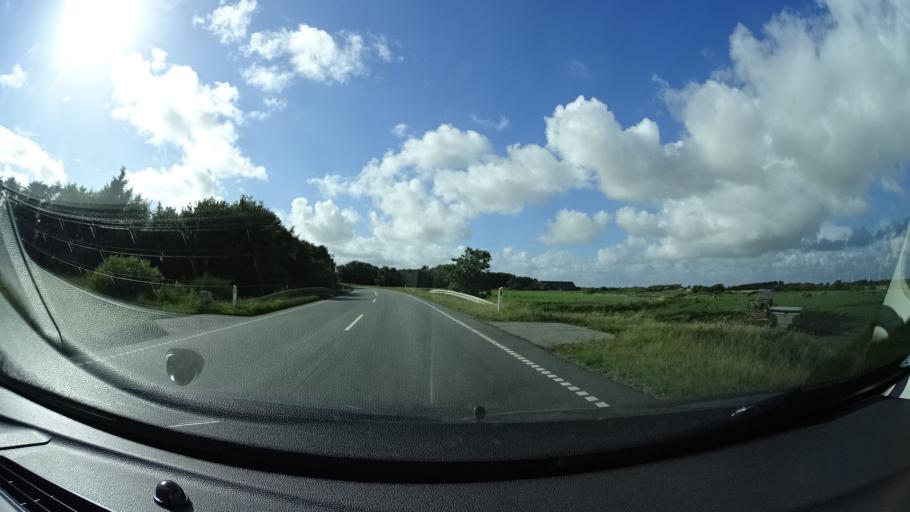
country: DK
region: South Denmark
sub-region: Varde Kommune
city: Oksbol
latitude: 55.7856
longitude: 8.2622
